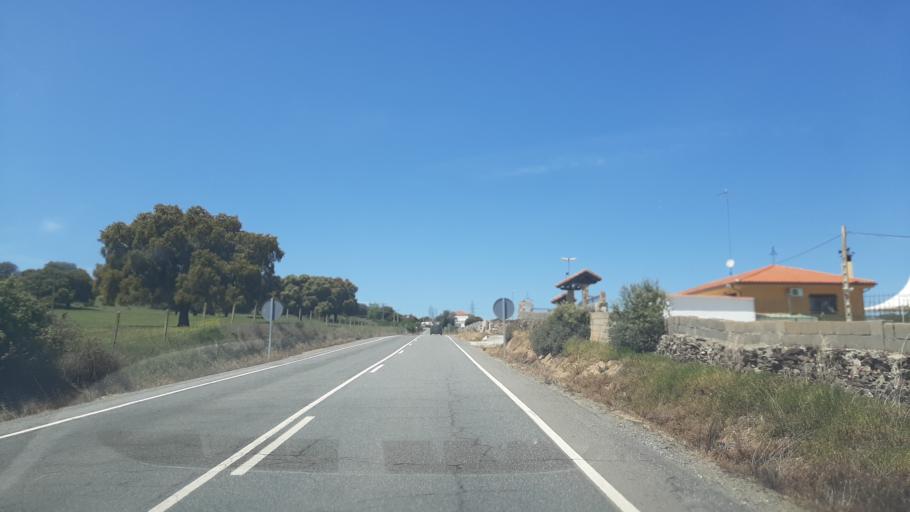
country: ES
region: Castille and Leon
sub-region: Provincia de Salamanca
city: Guijo de Avila
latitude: 40.5558
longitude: -5.6423
